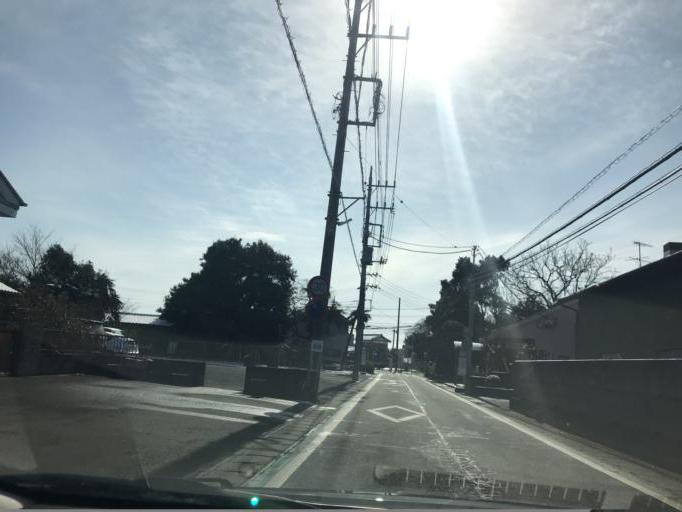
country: JP
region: Ibaraki
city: Moriya
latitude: 35.9524
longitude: 139.9569
